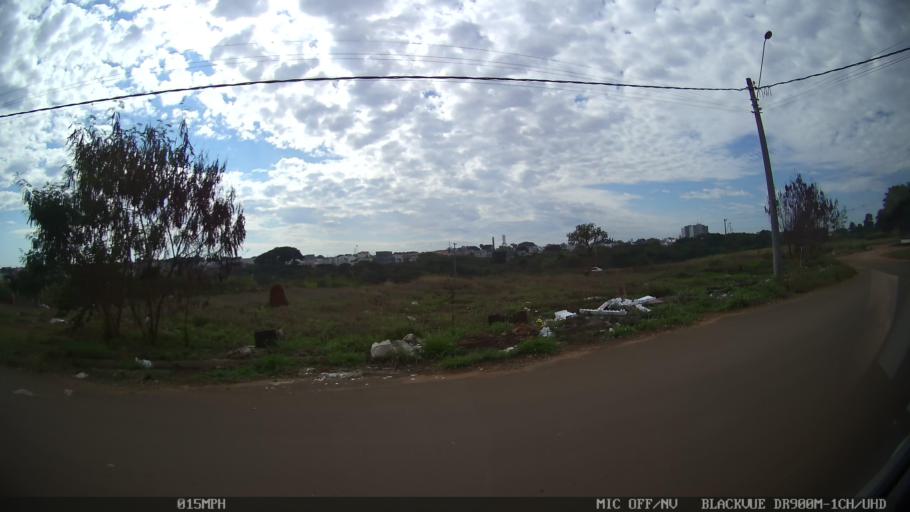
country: BR
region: Sao Paulo
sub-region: Americana
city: Americana
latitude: -22.7327
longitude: -47.3668
